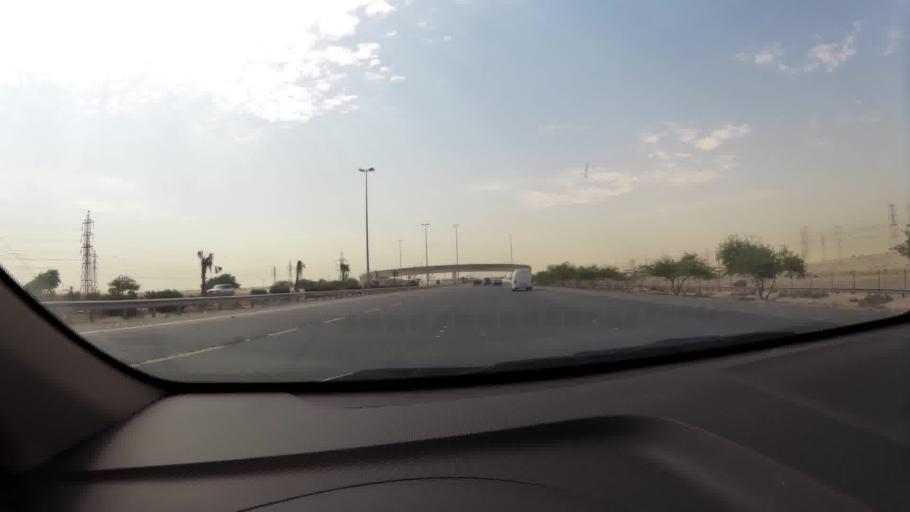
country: KW
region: Al Ahmadi
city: Al Fahahil
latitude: 28.8871
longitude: 48.2256
